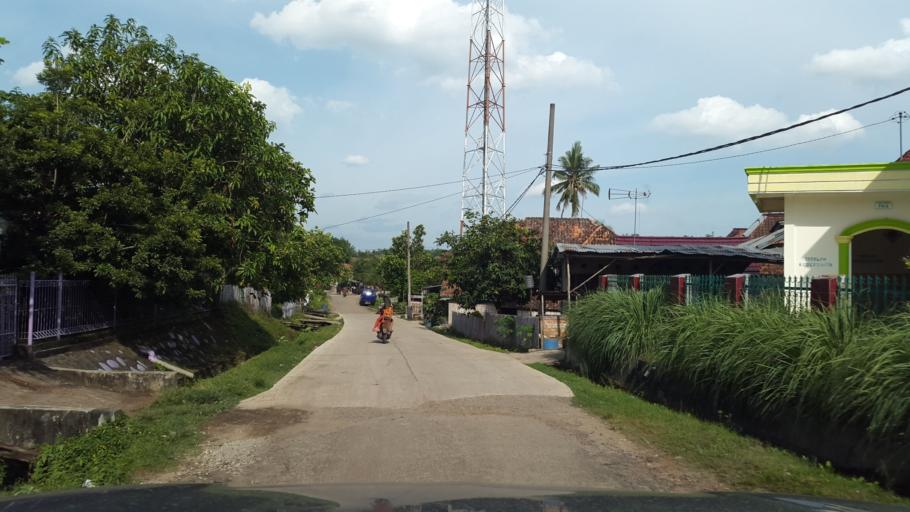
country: ID
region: South Sumatra
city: Prabumulih
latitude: -3.4386
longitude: 104.4091
